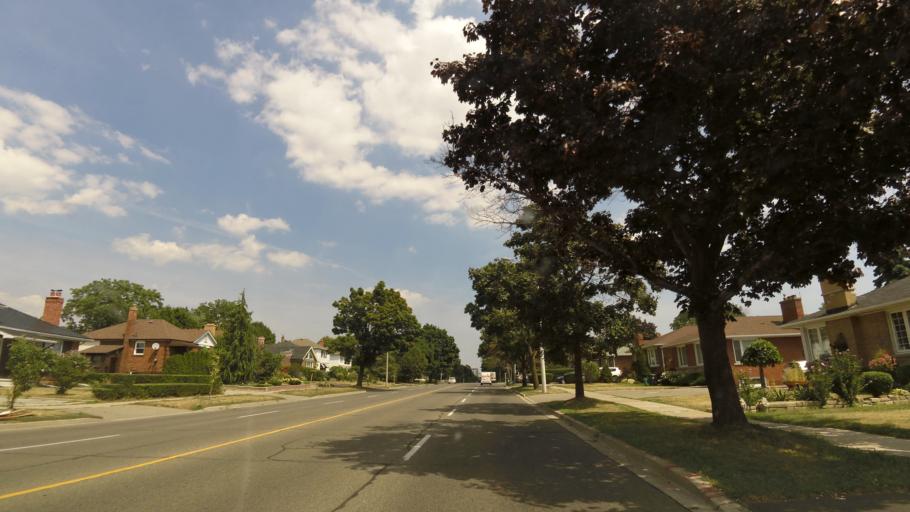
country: CA
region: Ontario
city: Etobicoke
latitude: 43.6376
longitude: -79.5536
